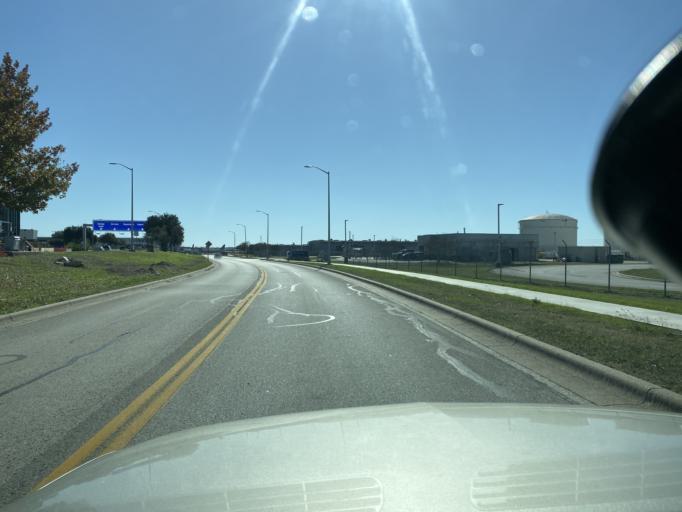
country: US
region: Texas
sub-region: Travis County
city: Austin
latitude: 30.2076
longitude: -97.6713
